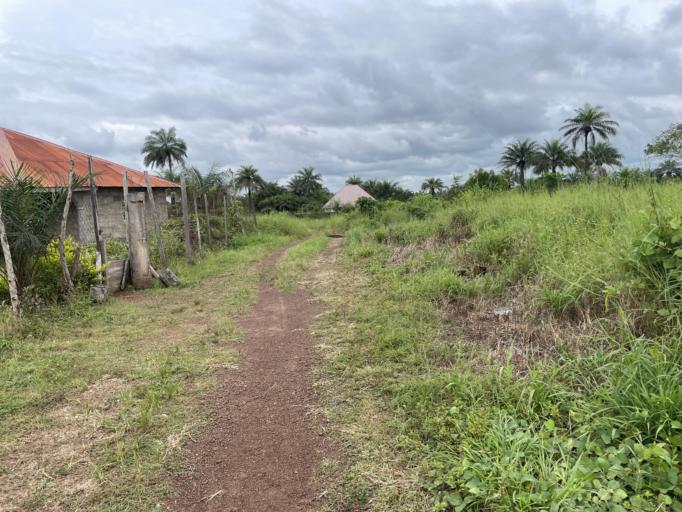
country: SL
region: Northern Province
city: Kambia
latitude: 9.1334
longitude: -12.9079
